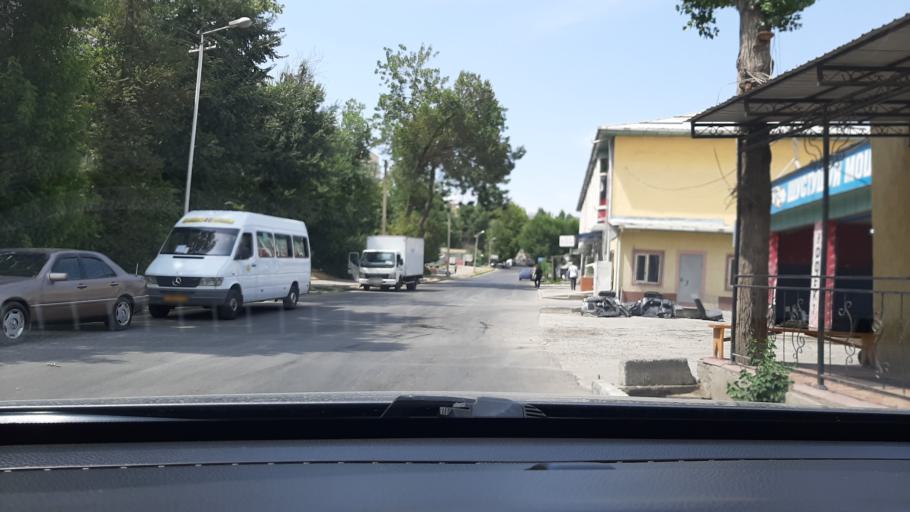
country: TJ
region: Dushanbe
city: Dushanbe
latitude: 38.5789
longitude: 68.7322
